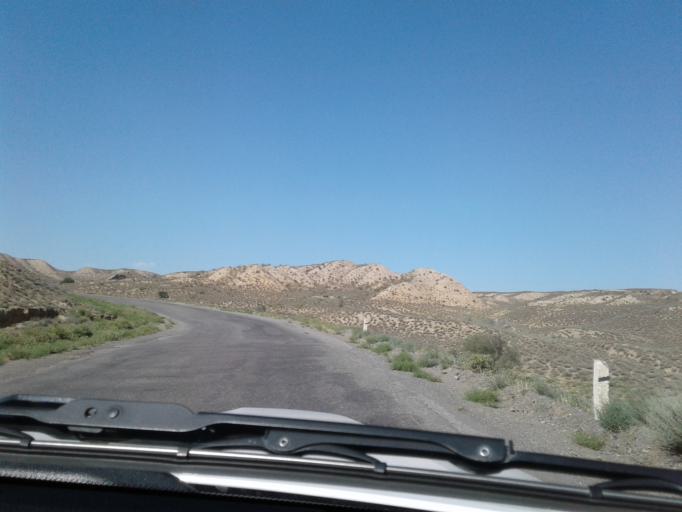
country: TM
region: Balkan
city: Magtymguly
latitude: 38.6509
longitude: 56.2756
